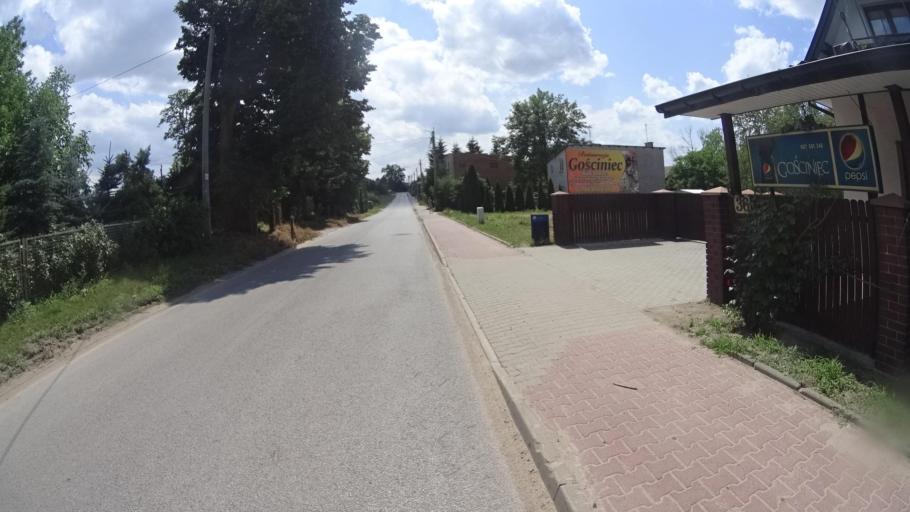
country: PL
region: Masovian Voivodeship
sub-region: Powiat grojecki
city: Goszczyn
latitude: 51.7276
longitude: 20.8507
